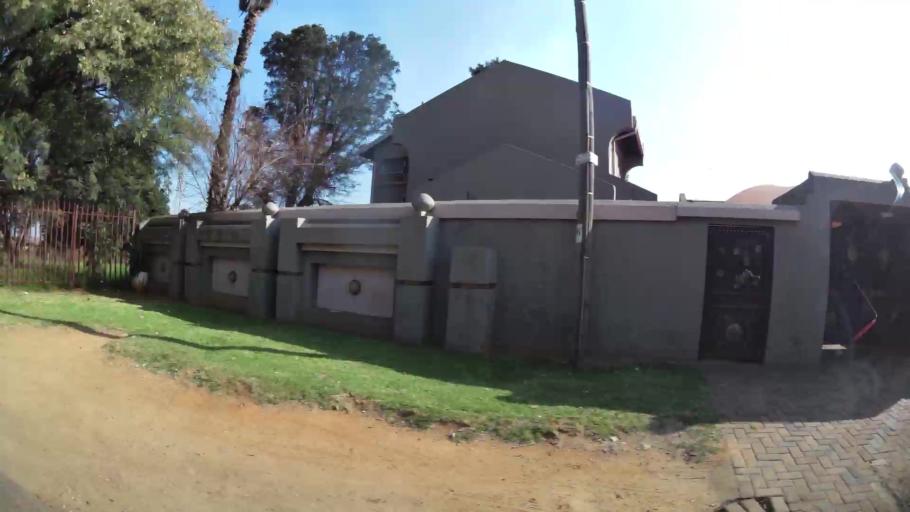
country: ZA
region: Gauteng
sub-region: Ekurhuleni Metropolitan Municipality
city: Benoni
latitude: -26.1544
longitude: 28.3983
